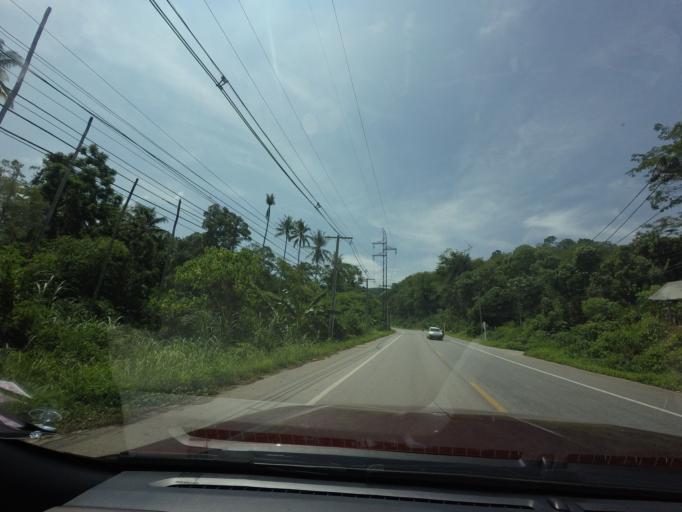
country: TH
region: Yala
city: Betong
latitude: 5.8186
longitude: 101.0980
